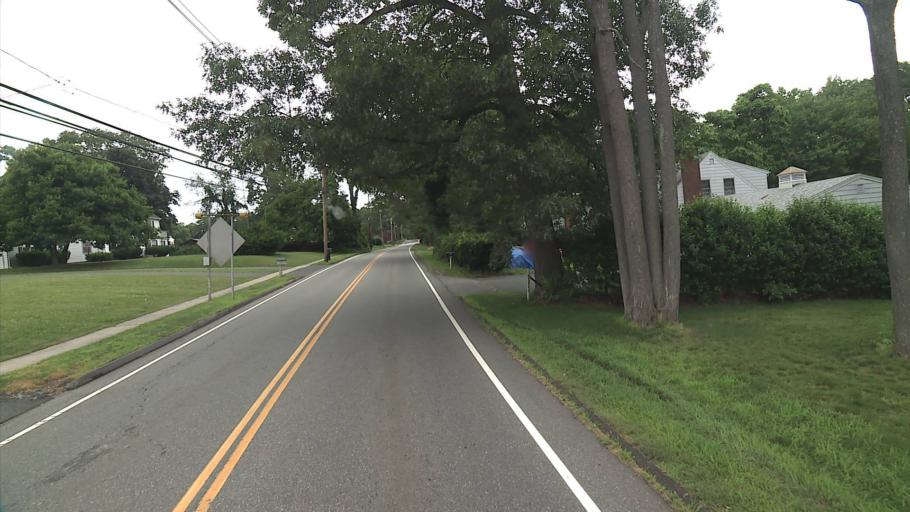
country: US
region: Connecticut
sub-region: New Haven County
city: Wallingford Center
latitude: 41.4381
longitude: -72.8048
